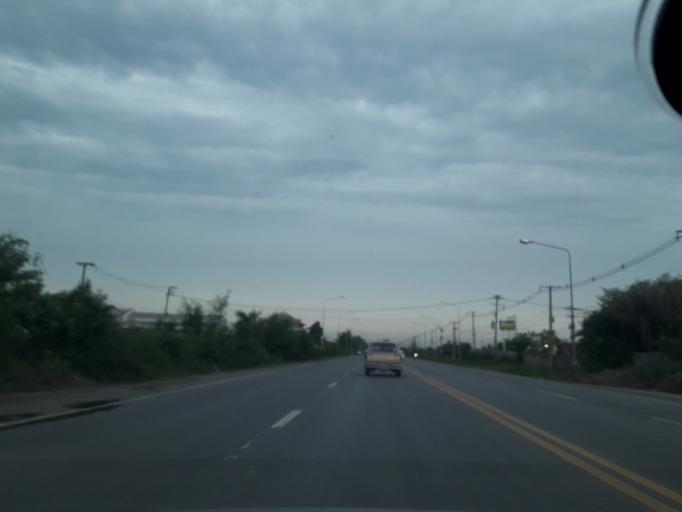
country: TH
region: Pathum Thani
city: Ban Rangsit
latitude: 14.0606
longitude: 100.7471
